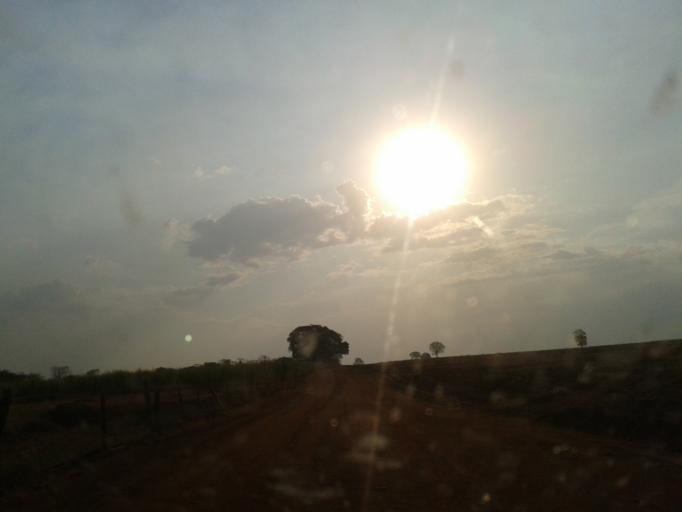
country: BR
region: Minas Gerais
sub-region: Capinopolis
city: Capinopolis
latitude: -18.7567
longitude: -49.6894
